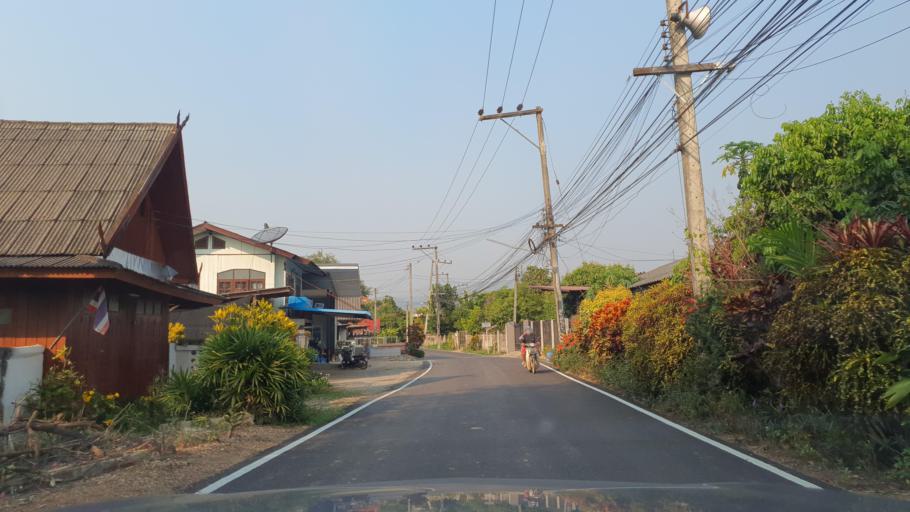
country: TH
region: Chiang Mai
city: Mae Taeng
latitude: 19.1378
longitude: 99.0096
